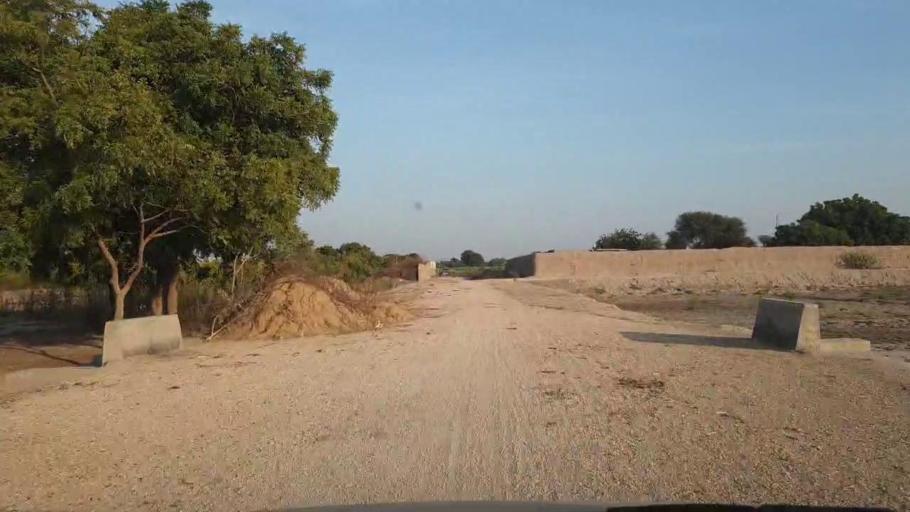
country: PK
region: Sindh
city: Chambar
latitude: 25.2584
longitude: 68.7994
